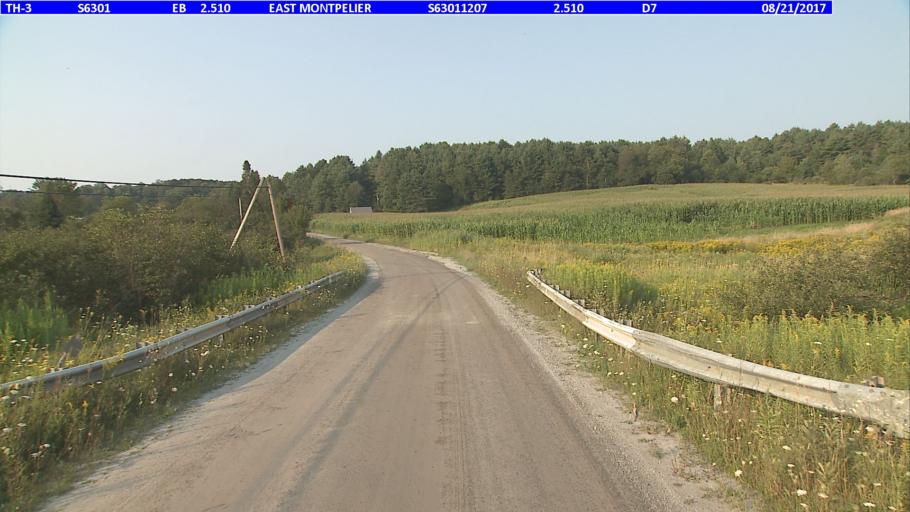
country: US
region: Vermont
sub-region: Washington County
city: Montpelier
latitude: 44.2942
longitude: -72.5180
